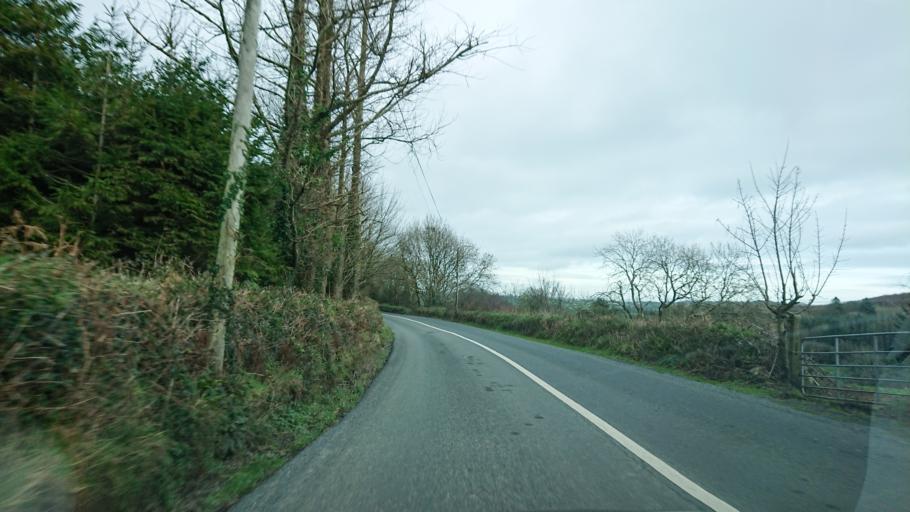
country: IE
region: Leinster
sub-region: Kilkenny
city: Mooncoin
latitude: 52.2074
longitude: -7.2482
